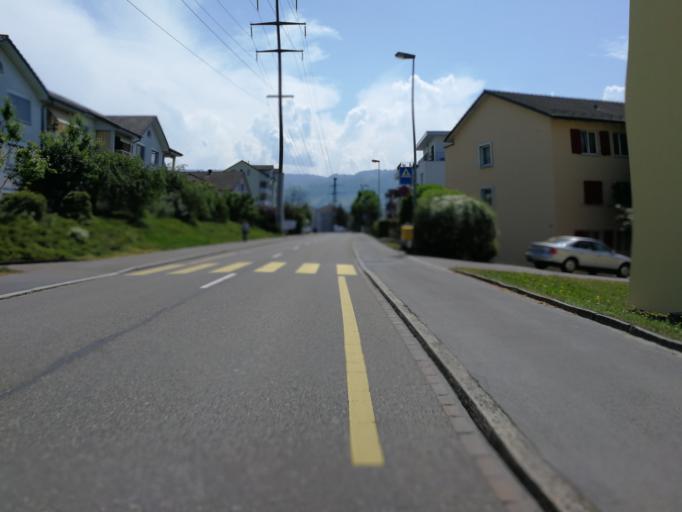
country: CH
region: Saint Gallen
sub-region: Wahlkreis See-Gaster
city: Jona
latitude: 47.2269
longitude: 8.8330
